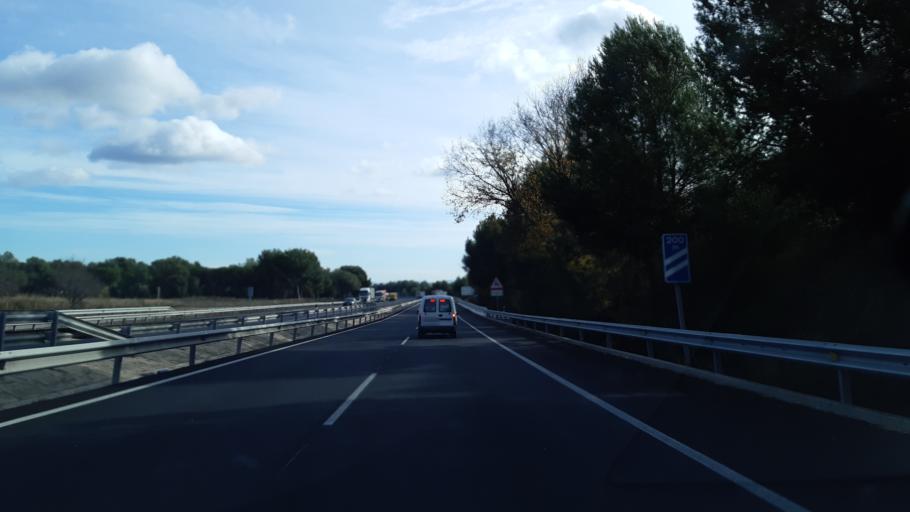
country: ES
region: Catalonia
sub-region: Provincia de Barcelona
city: Collbato
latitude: 41.5711
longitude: 1.7935
